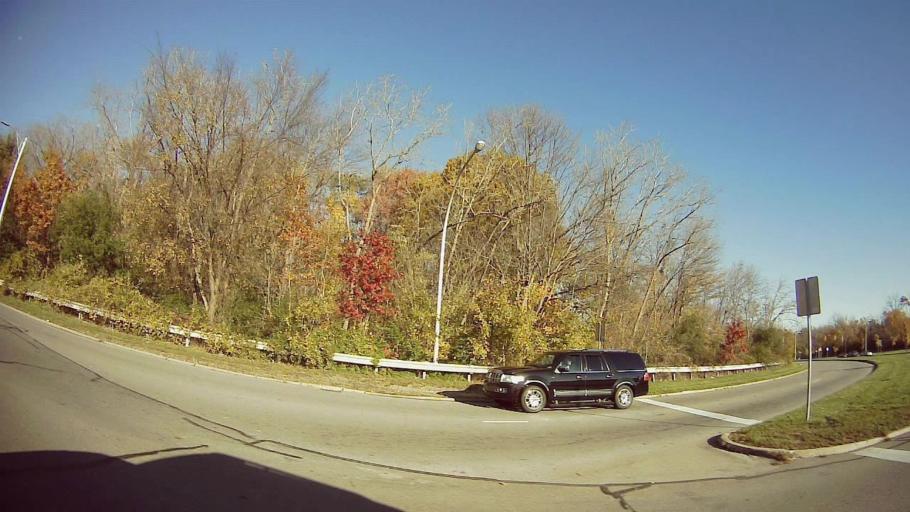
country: US
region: Michigan
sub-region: Wayne County
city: Dearborn
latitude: 42.3091
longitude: -83.2271
